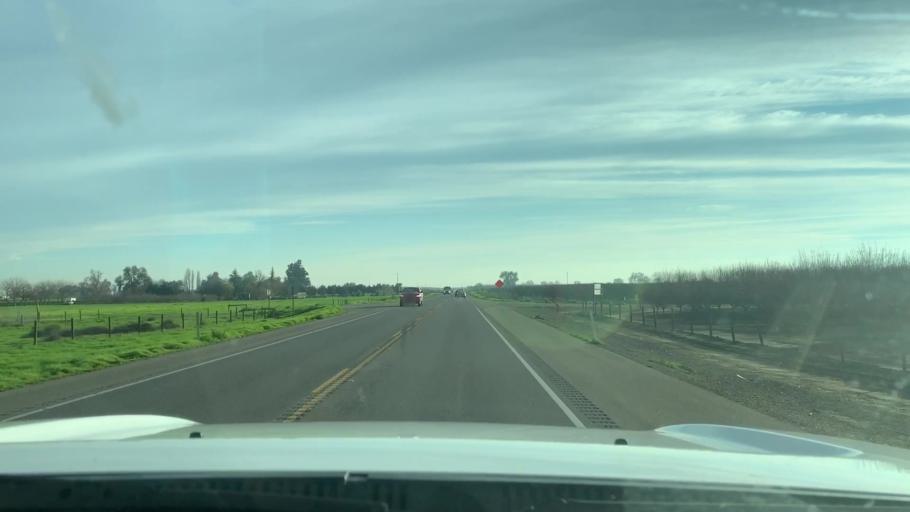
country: US
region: California
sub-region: Fresno County
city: Riverdale
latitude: 36.4173
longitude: -119.8040
